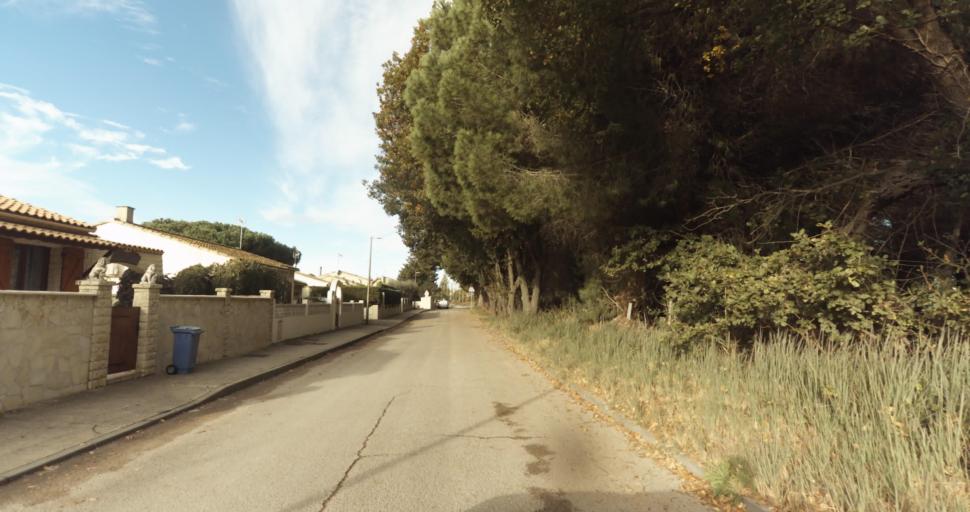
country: FR
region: Languedoc-Roussillon
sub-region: Departement du Gard
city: Aigues-Mortes
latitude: 43.5701
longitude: 4.2029
